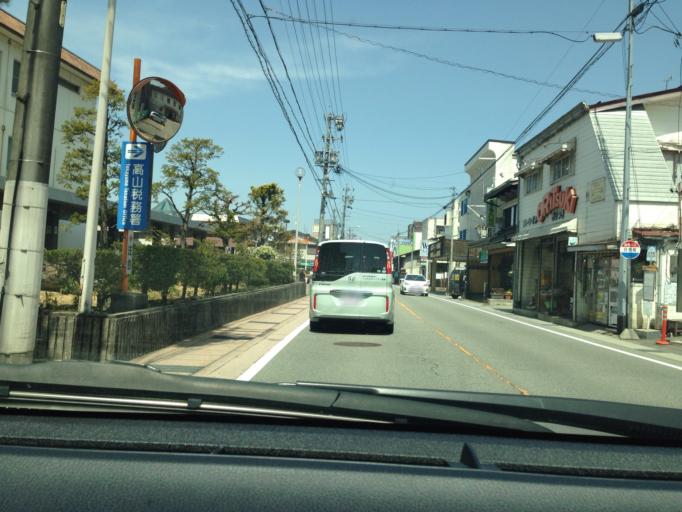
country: JP
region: Gifu
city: Takayama
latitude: 36.1368
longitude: 137.2551
